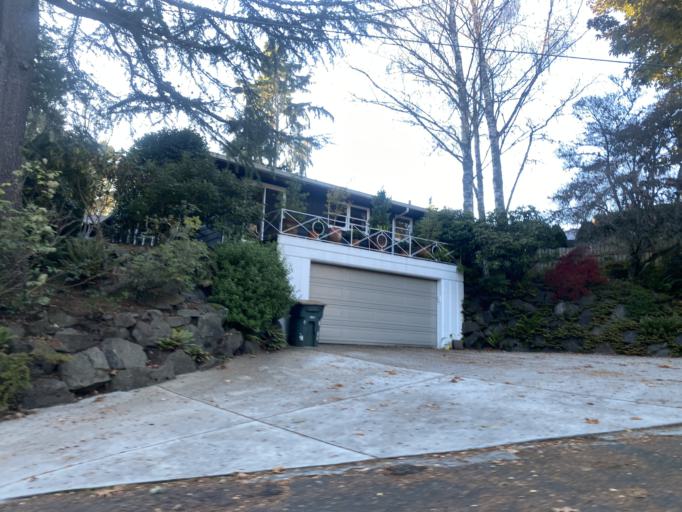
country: US
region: Washington
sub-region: King County
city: Seattle
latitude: 47.6537
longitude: -122.4161
